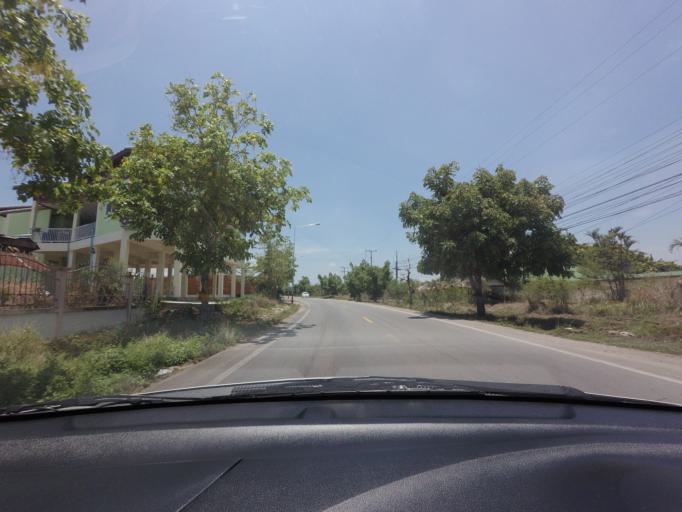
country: TH
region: Suphan Buri
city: Dan Chang
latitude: 14.8479
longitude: 99.7038
